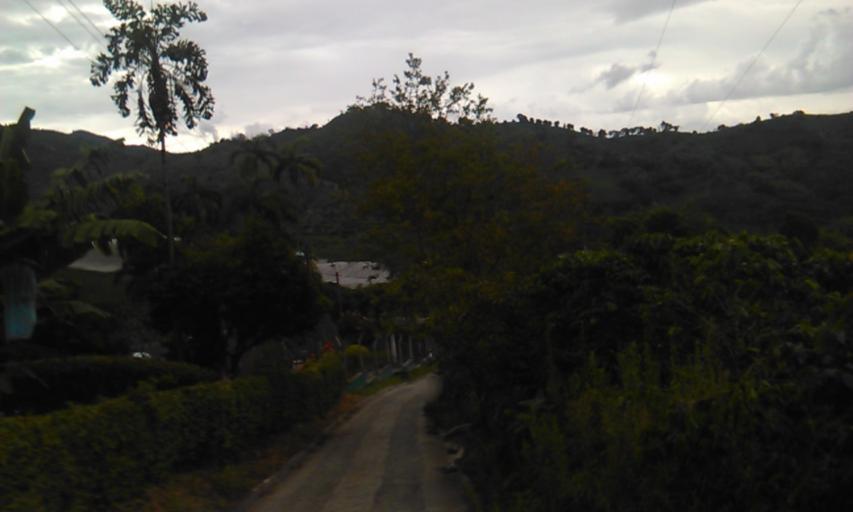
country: CO
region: Quindio
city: Cordoba
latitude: 4.4108
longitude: -75.6857
